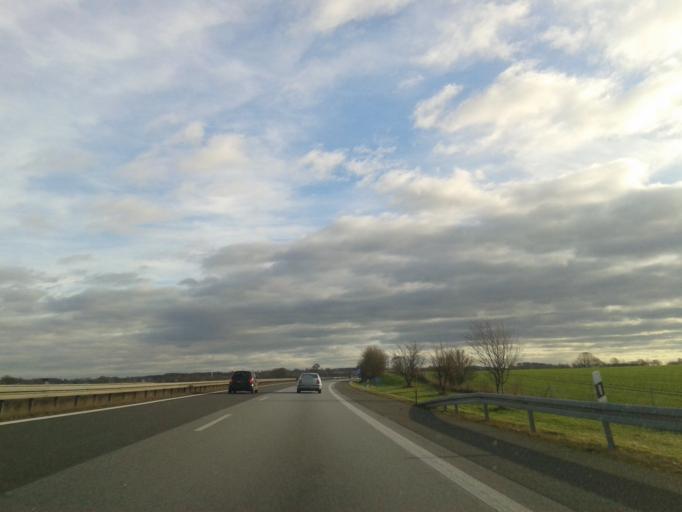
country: DE
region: Saxony
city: Goda
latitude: 51.2023
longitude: 14.3173
